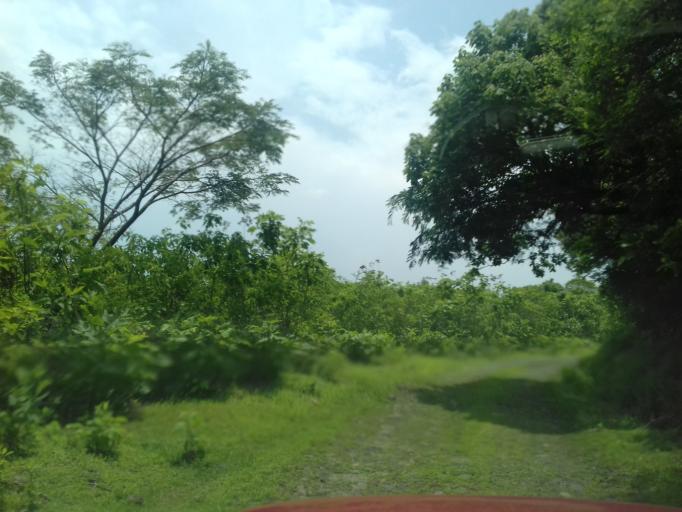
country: MX
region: Nayarit
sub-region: Ahuacatlan
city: Ahuacatlan
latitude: 21.1066
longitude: -104.4909
